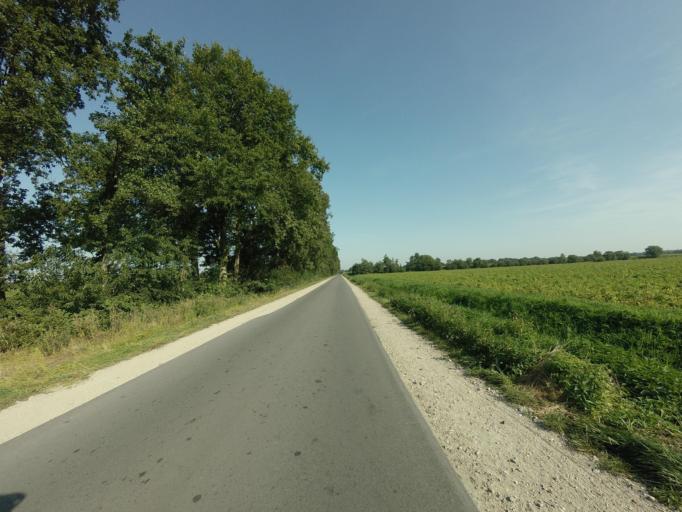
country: DE
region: Lower Saxony
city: Laar
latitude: 52.5830
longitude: 6.7798
